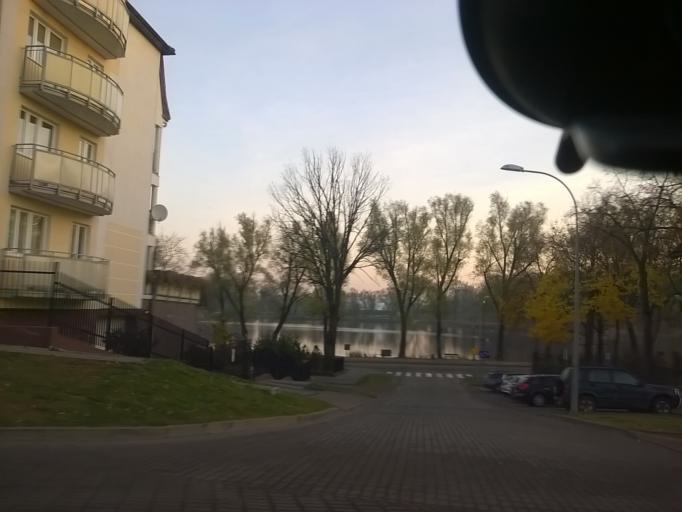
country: PL
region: Warmian-Masurian Voivodeship
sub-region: Powiat ketrzynski
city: Ketrzyn
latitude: 54.0782
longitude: 21.3757
